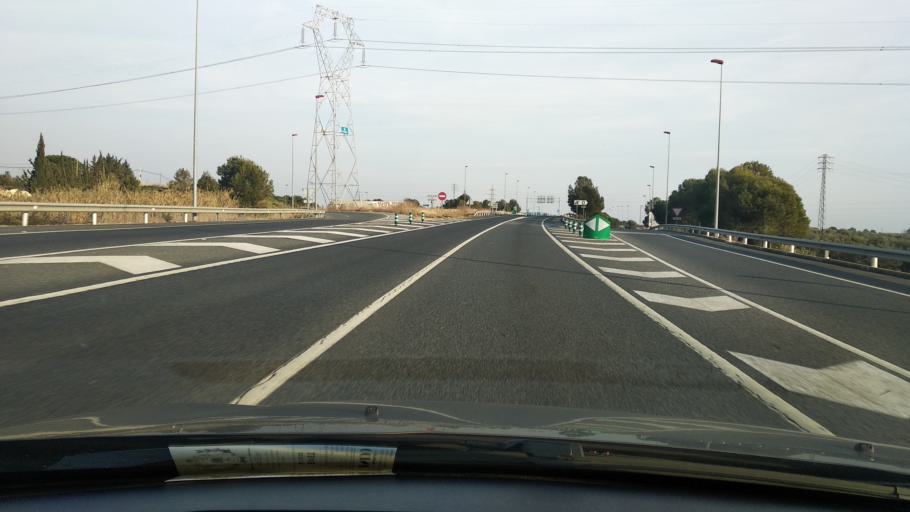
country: ES
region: Catalonia
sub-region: Provincia de Tarragona
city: Riudoms
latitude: 41.1659
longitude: 1.0564
